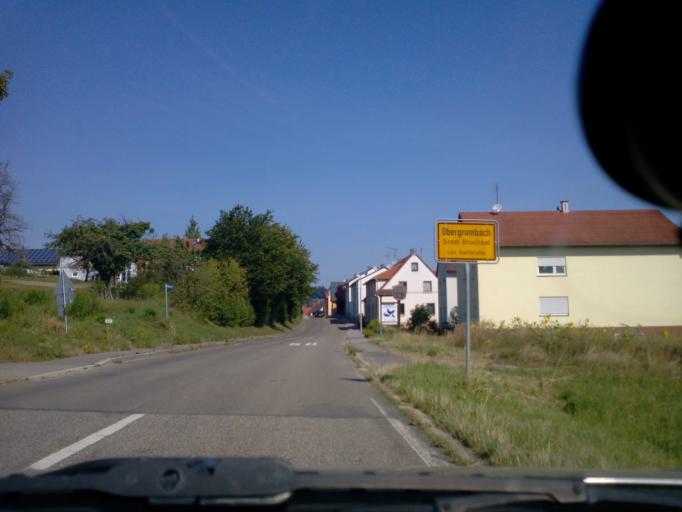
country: DE
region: Baden-Wuerttemberg
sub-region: Karlsruhe Region
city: Joehlingen
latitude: 49.0730
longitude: 8.5907
